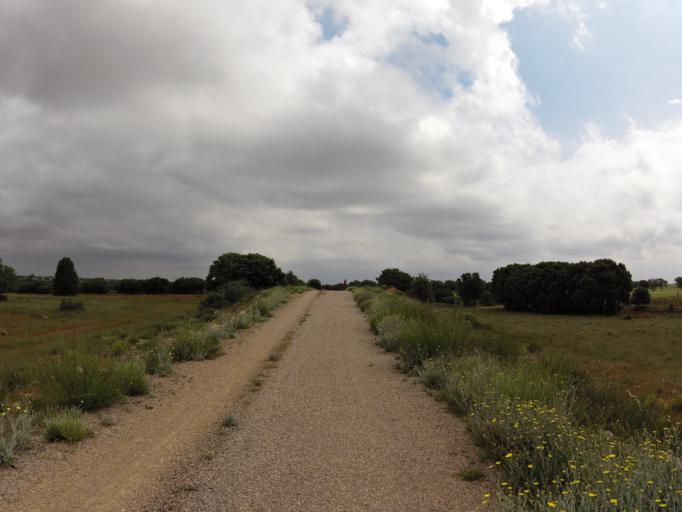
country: ES
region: Castille-La Mancha
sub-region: Provincia de Albacete
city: Robledo
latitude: 38.7616
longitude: -2.4638
